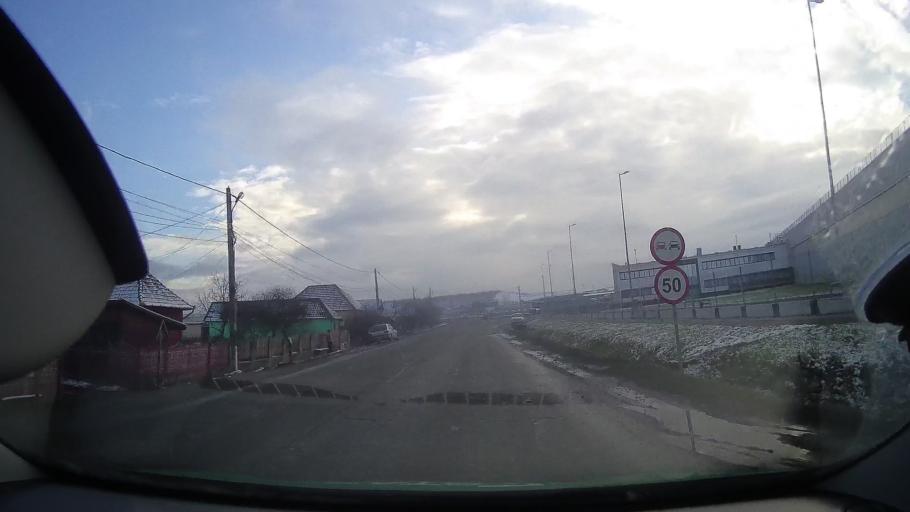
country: RO
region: Mures
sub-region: Comuna Iernut
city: Iernut
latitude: 46.4363
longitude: 24.2529
